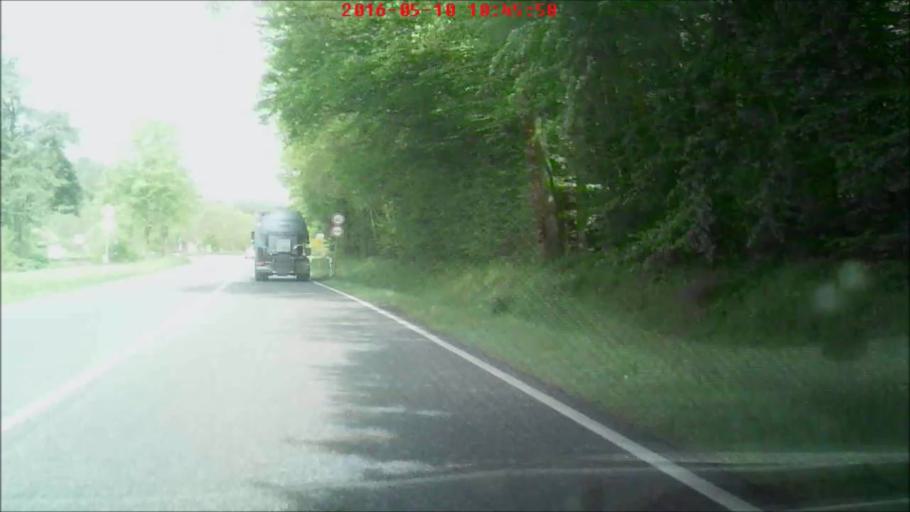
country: DE
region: Hesse
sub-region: Regierungsbezirk Kassel
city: Burghaun
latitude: 50.7369
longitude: 9.6927
